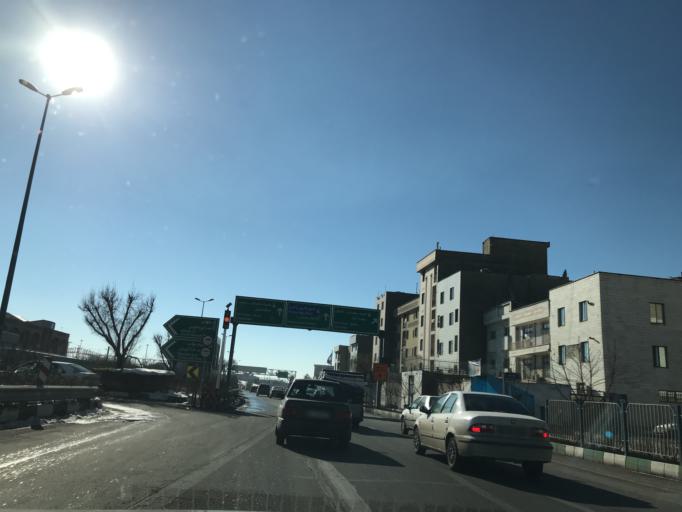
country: IR
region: Tehran
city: Tehran
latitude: 35.6392
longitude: 51.3611
